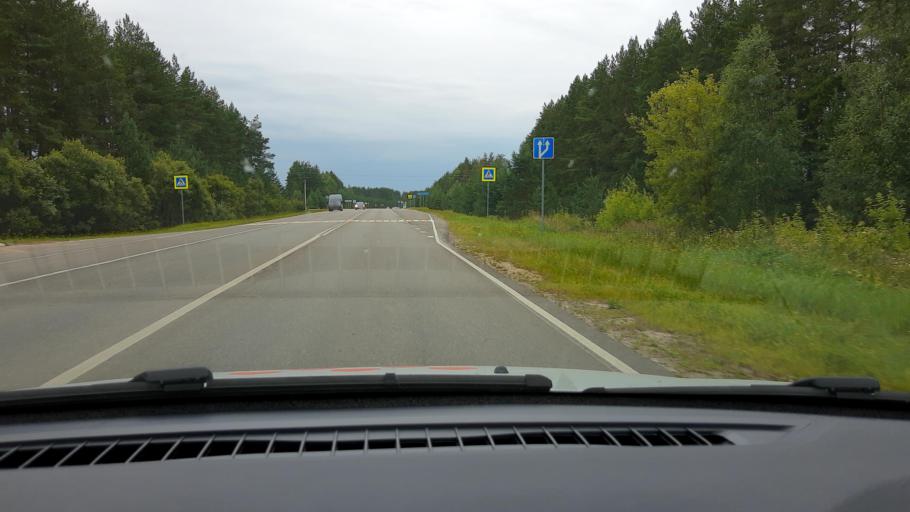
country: RU
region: Nizjnij Novgorod
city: Vyyezdnoye
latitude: 55.1963
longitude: 43.6192
